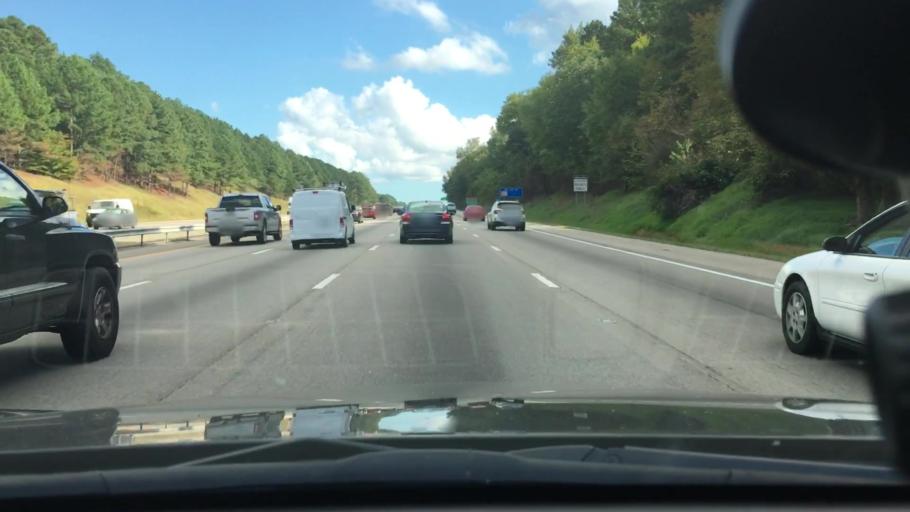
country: US
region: North Carolina
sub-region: Wake County
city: Cary
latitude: 35.8361
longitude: -78.7736
